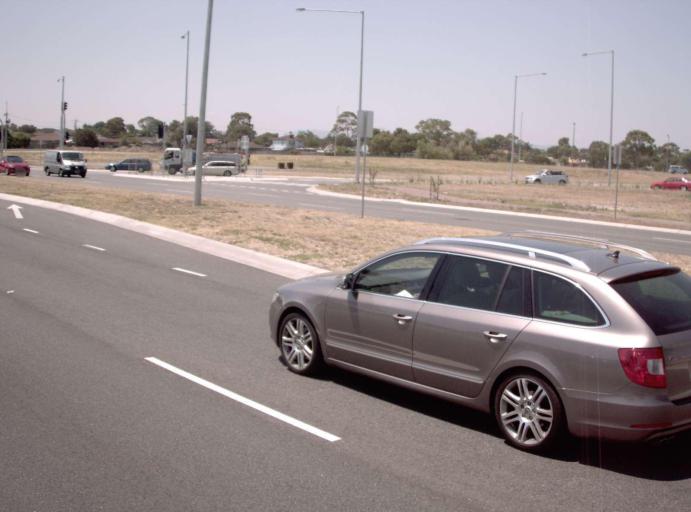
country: AU
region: Victoria
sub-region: Kingston
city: Dingley Village
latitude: -37.9845
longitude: 145.1456
